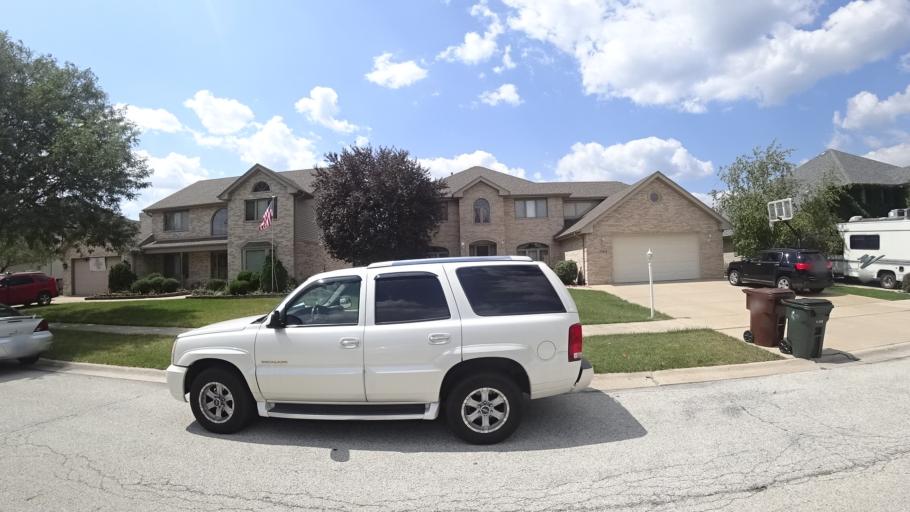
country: US
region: Illinois
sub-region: Cook County
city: Oak Forest
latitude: 41.6179
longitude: -87.7718
